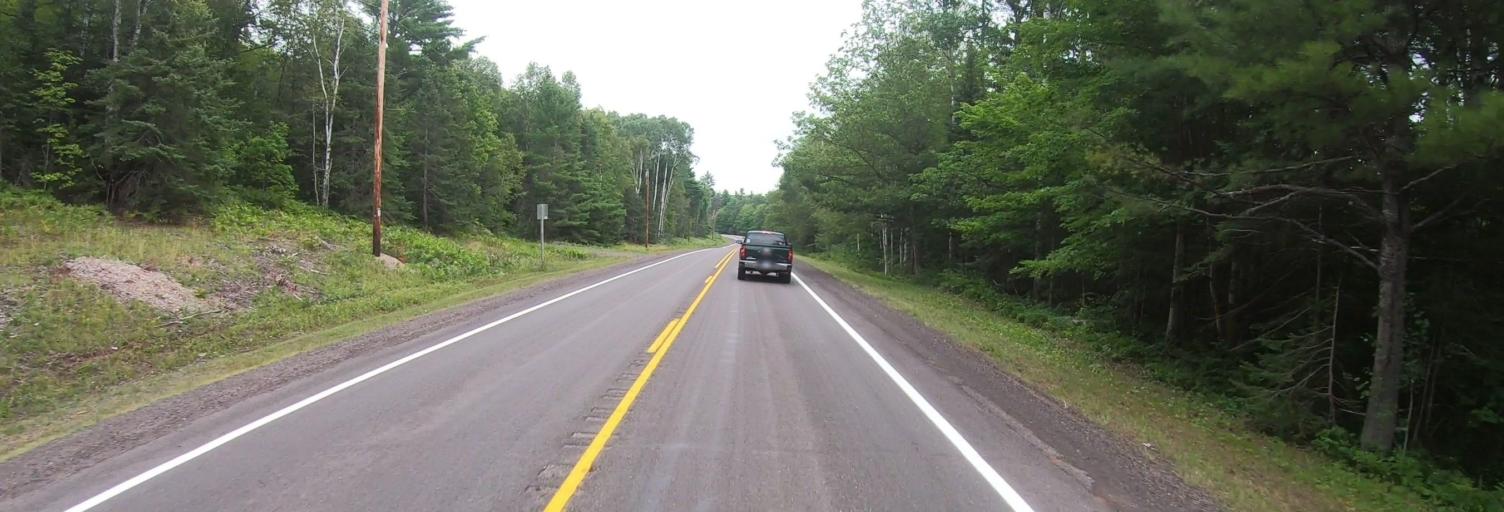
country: US
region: Michigan
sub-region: Keweenaw County
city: Eagle River
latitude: 47.4138
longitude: -88.1618
